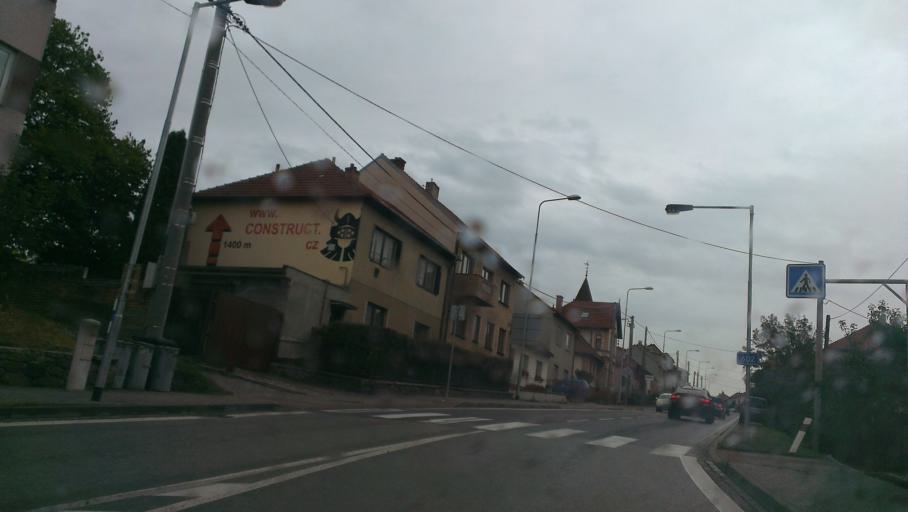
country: CZ
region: Vysocina
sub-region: Okres Zd'ar nad Sazavou
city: Velke Mezirici
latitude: 49.3495
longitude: 16.0243
